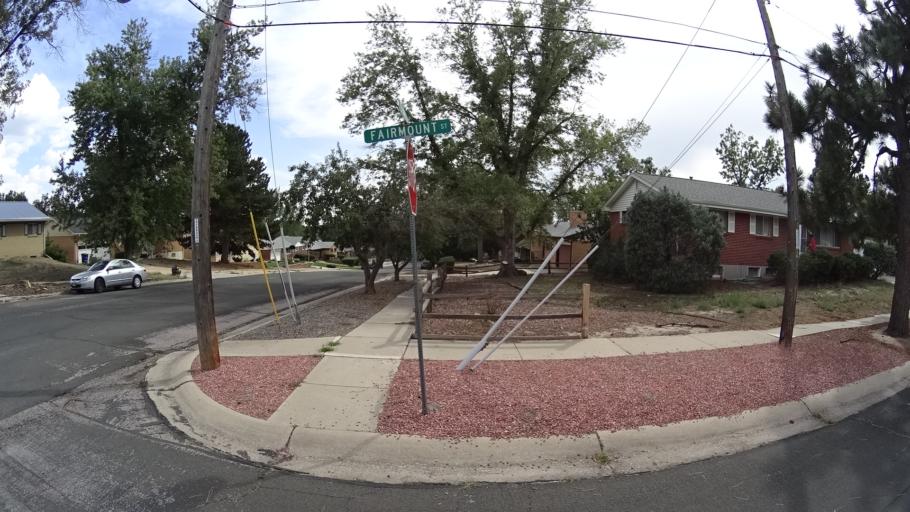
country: US
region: Colorado
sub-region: El Paso County
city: Colorado Springs
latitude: 38.8647
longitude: -104.7771
